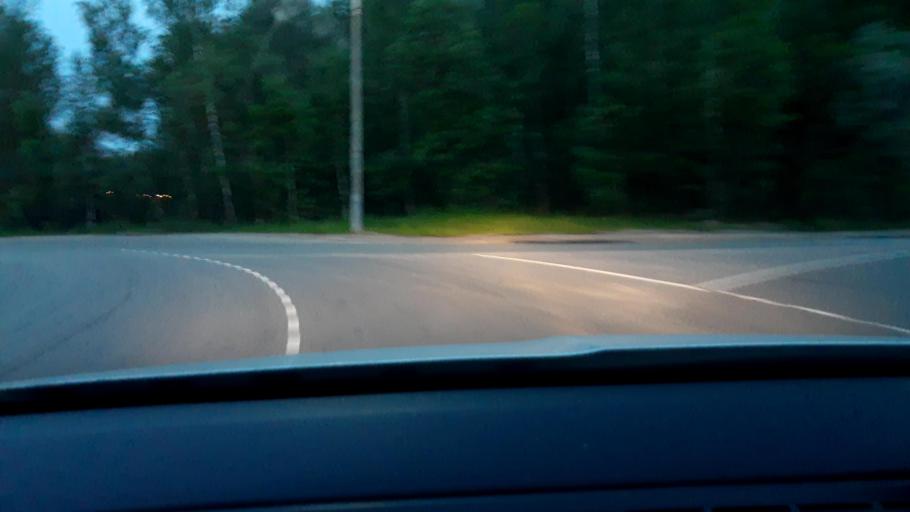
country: RU
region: Moskovskaya
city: Obolensk
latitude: 54.9796
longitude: 37.2516
